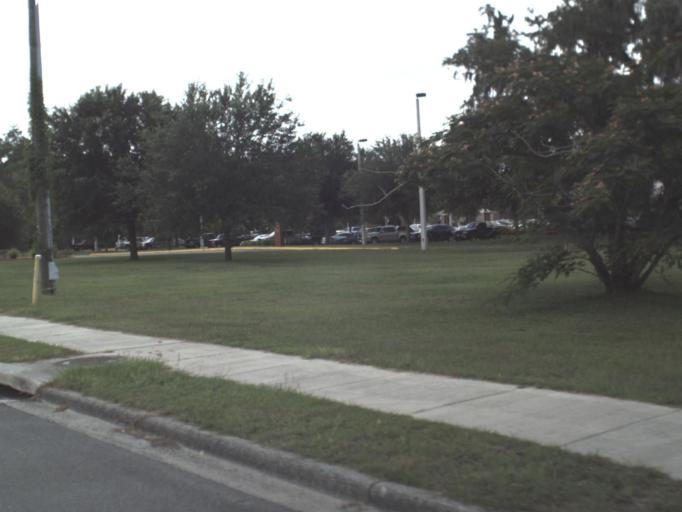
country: US
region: Florida
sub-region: Taylor County
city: Perry
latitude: 30.1217
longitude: -83.5925
